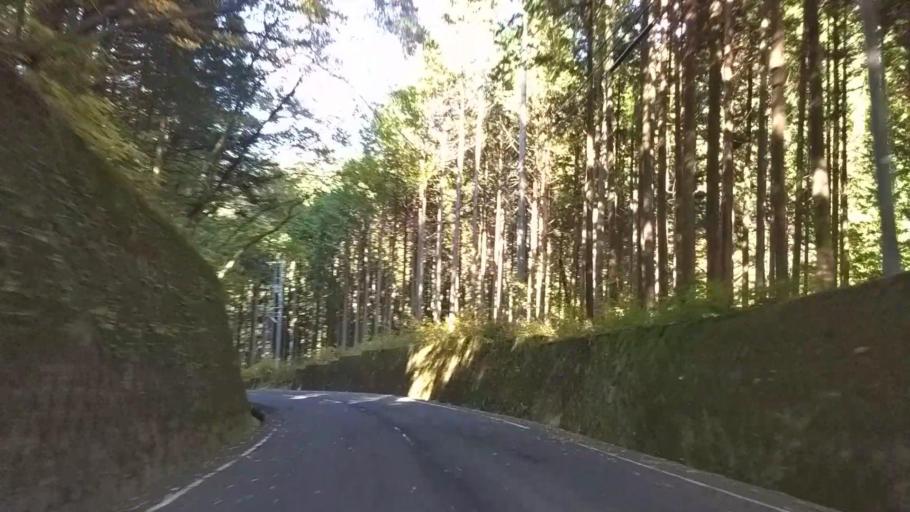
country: JP
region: Yamanashi
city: Otsuki
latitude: 35.7418
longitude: 138.9669
